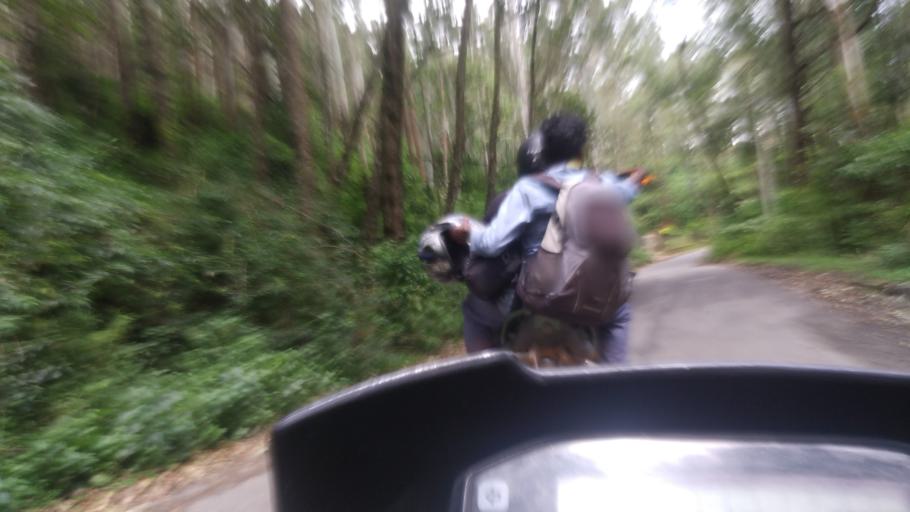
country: IN
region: Kerala
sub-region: Idukki
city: Munnar
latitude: 10.0714
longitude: 77.0981
